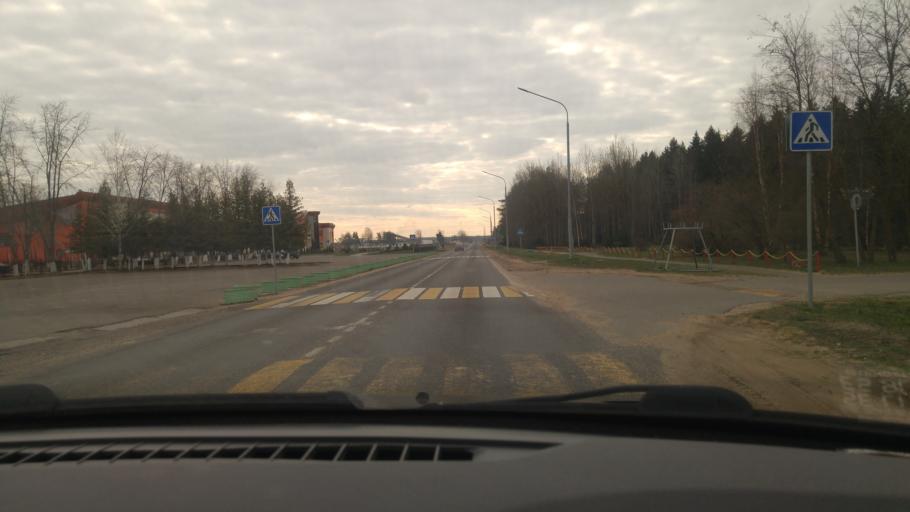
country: BY
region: Minsk
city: Chervyen'
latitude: 53.7003
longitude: 28.4155
